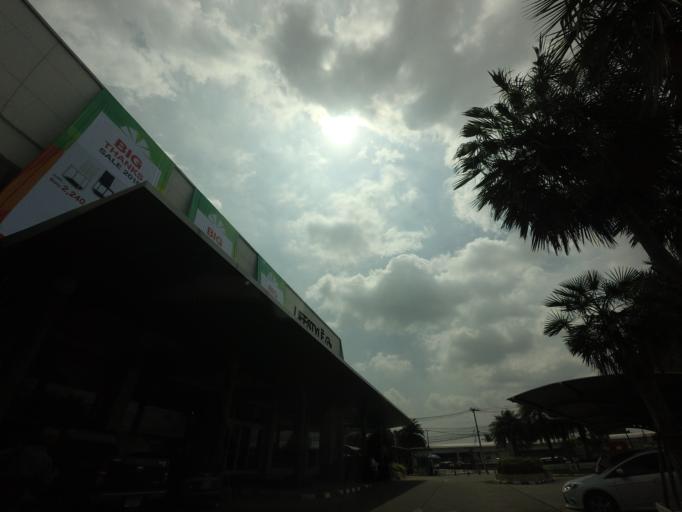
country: TH
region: Bangkok
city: Lat Phrao
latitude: 13.8211
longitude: 100.6343
